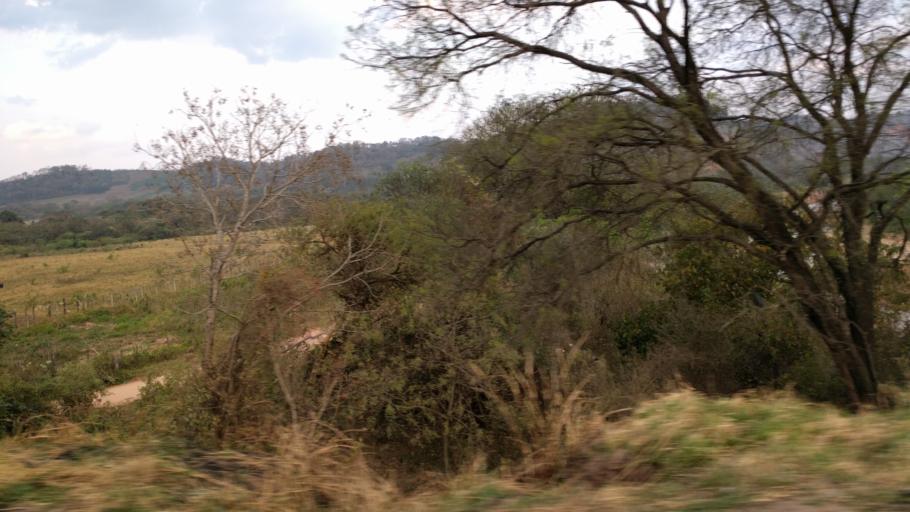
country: BO
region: Santa Cruz
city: Jorochito
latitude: -18.1079
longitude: -63.4574
